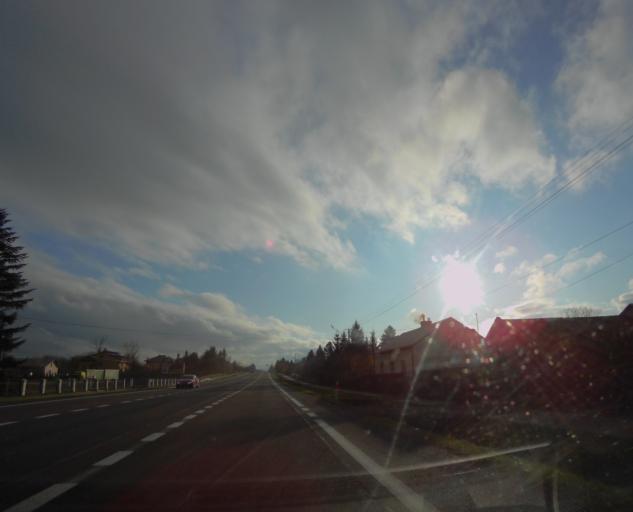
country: PL
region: Subcarpathian Voivodeship
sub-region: Powiat przemyski
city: Orly
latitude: 49.8642
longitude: 22.8085
